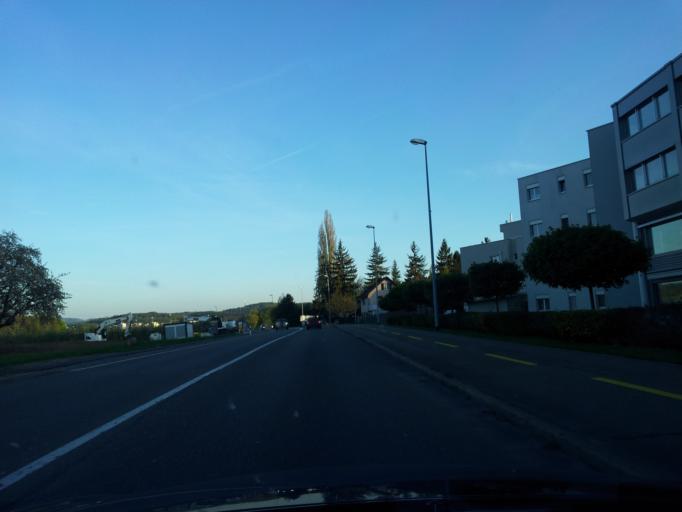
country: CH
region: Aargau
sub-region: Bezirk Baden
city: Spreitenbach
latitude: 47.4172
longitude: 8.3757
